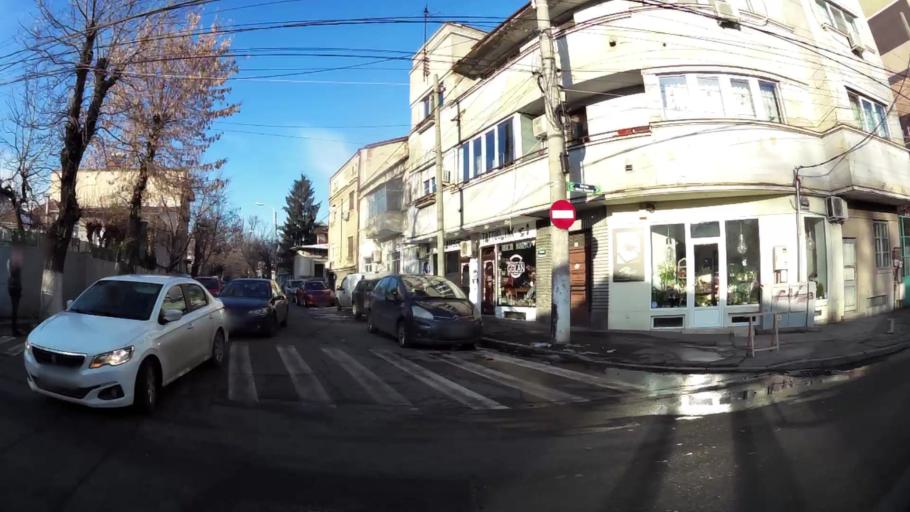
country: RO
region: Bucuresti
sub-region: Municipiul Bucuresti
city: Bucharest
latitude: 44.4375
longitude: 26.1296
